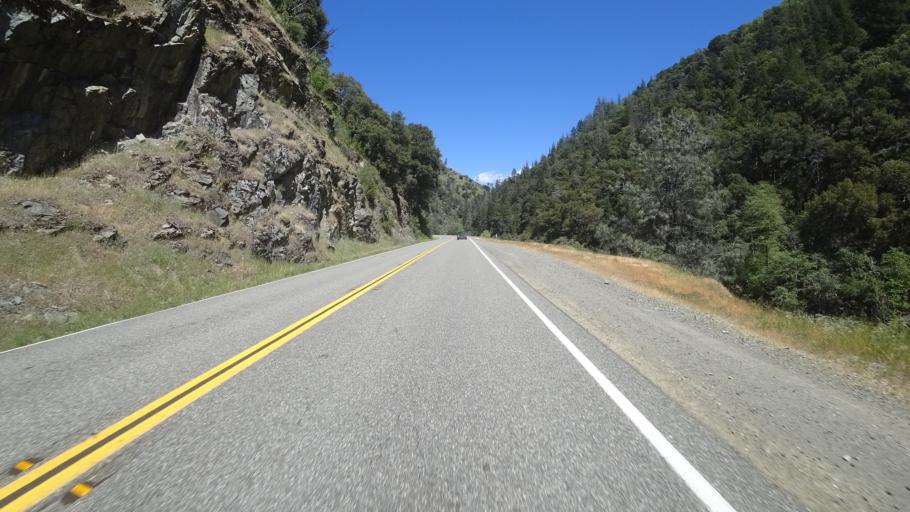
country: US
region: California
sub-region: Trinity County
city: Hayfork
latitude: 40.7484
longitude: -123.1700
